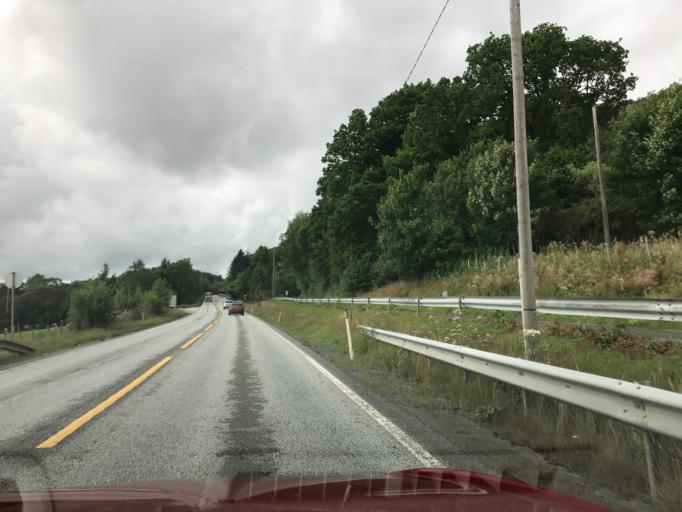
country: NO
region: Rogaland
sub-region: Tysvaer
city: Aksdal
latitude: 59.4226
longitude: 5.4222
